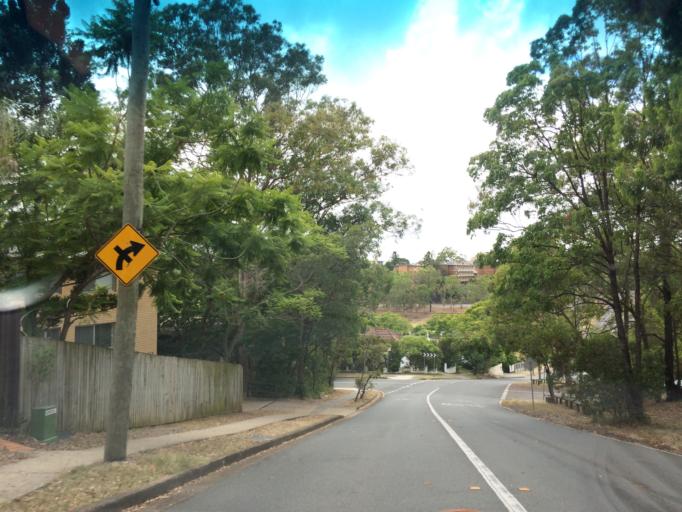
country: AU
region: Queensland
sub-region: Brisbane
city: Toowong
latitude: -27.4979
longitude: 153.0037
